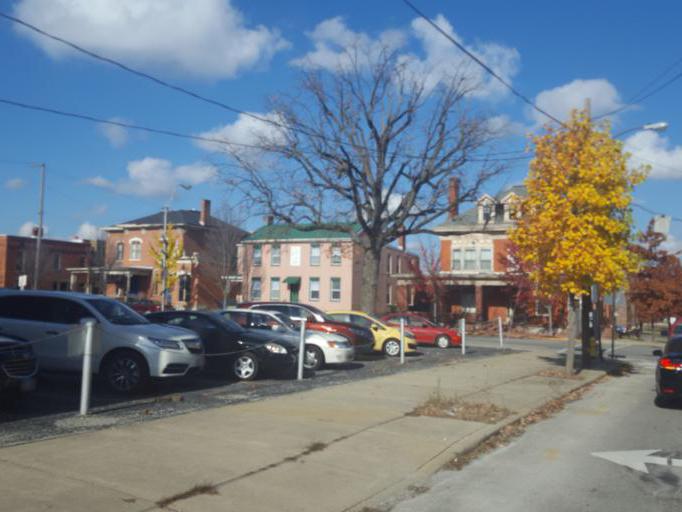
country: US
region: Ohio
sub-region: Seneca County
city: Tiffin
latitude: 41.1156
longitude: -83.1751
